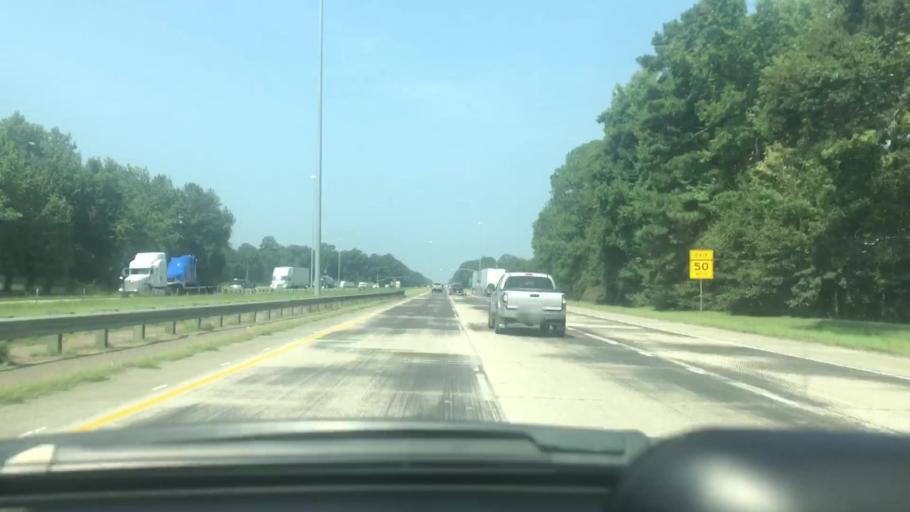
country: US
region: Louisiana
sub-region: Tangipahoa Parish
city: Hammond
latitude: 30.4796
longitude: -90.5172
